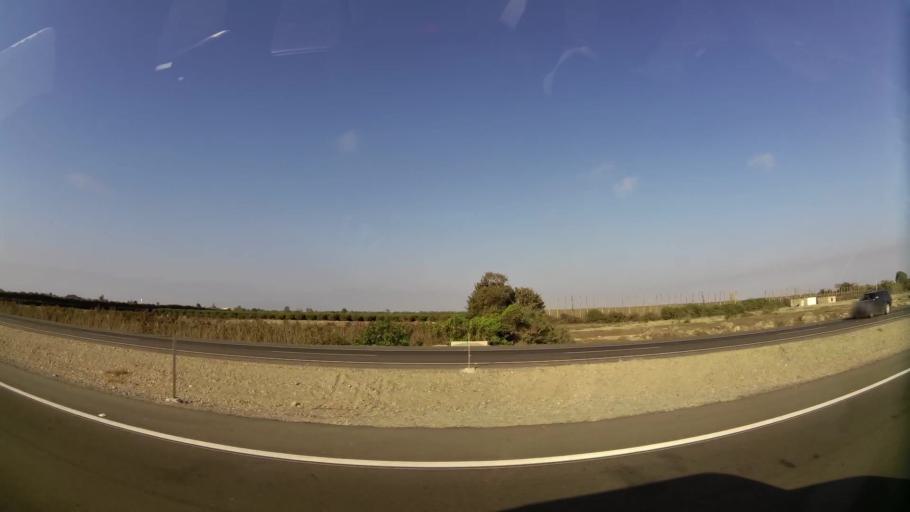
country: PE
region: Ica
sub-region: Provincia de Chincha
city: Chincha Baja
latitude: -13.4862
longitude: -76.1847
